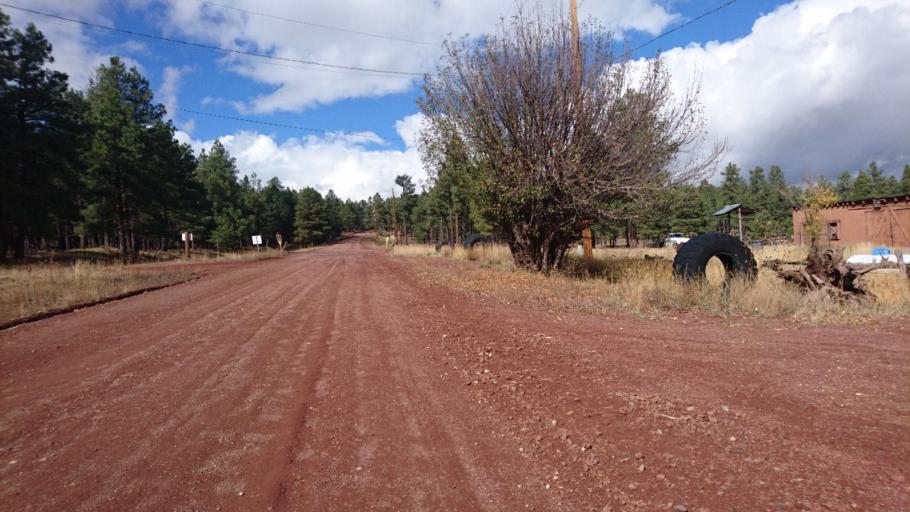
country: US
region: Arizona
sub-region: Coconino County
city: Parks
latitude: 35.2729
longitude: -111.8937
